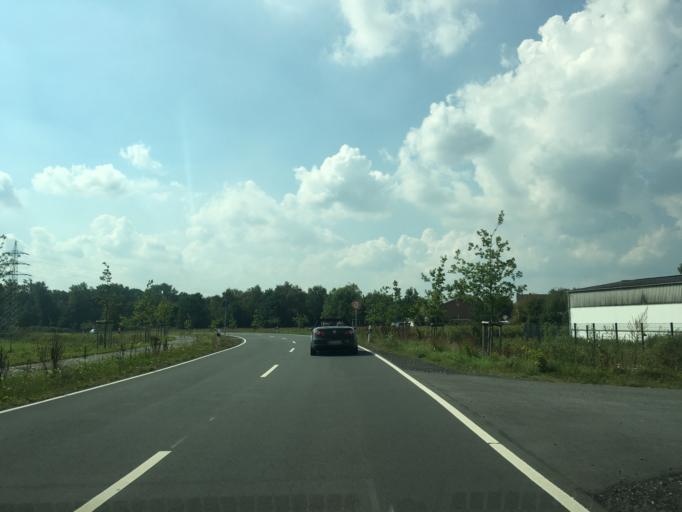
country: DE
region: North Rhine-Westphalia
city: Selm
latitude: 51.6865
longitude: 7.4806
